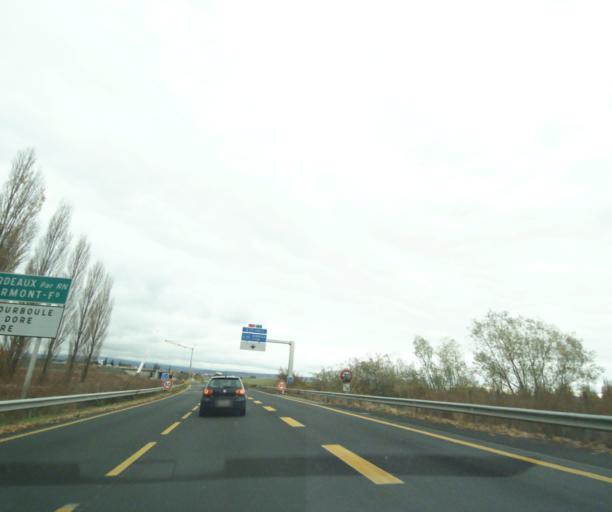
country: FR
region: Auvergne
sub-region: Departement du Puy-de-Dome
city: Perignat-les-Sarlieve
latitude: 45.7400
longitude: 3.1491
